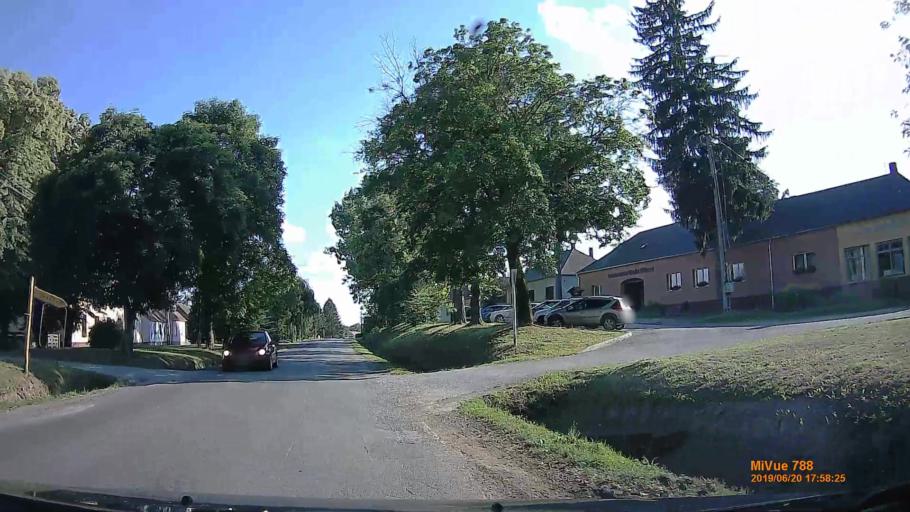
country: HU
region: Baranya
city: Buekkoesd
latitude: 46.1046
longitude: 17.9908
